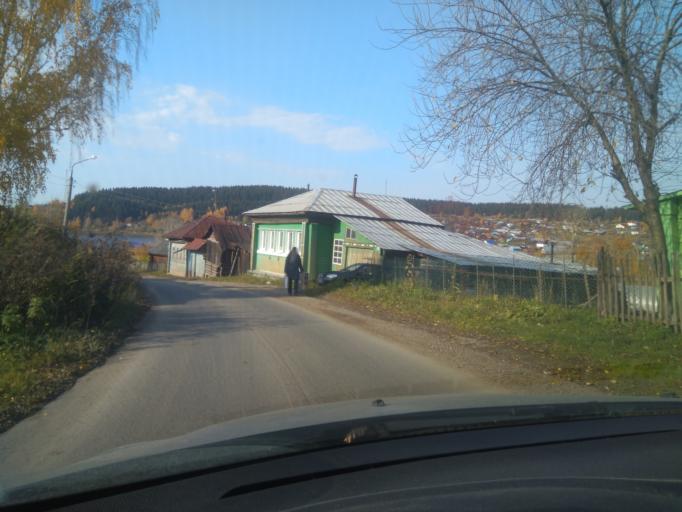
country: RU
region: Sverdlovsk
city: Nizhniye Sergi
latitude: 56.6769
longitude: 59.3338
